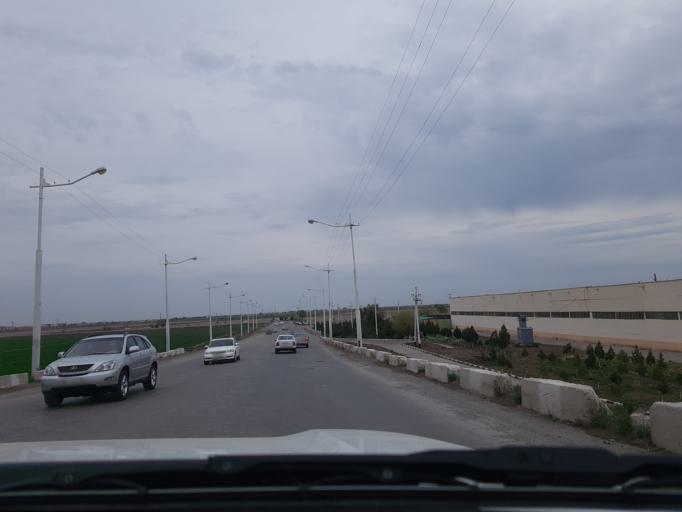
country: TM
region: Lebap
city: Turkmenabat
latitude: 39.0723
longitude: 63.5697
